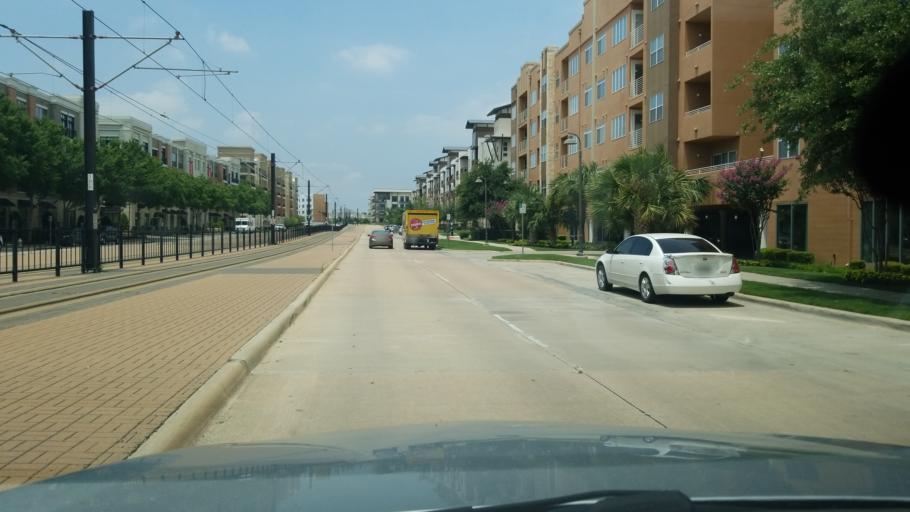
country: US
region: Texas
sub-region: Dallas County
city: Irving
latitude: 32.8711
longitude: -96.9349
